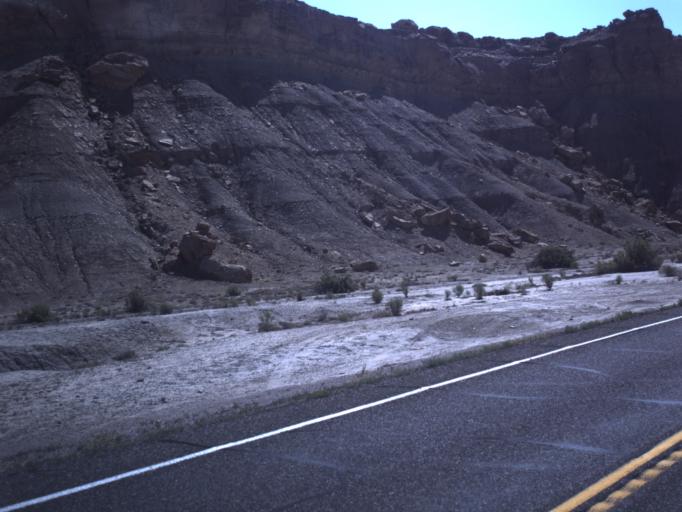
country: US
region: Utah
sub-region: Wayne County
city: Loa
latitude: 38.3642
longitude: -110.8783
